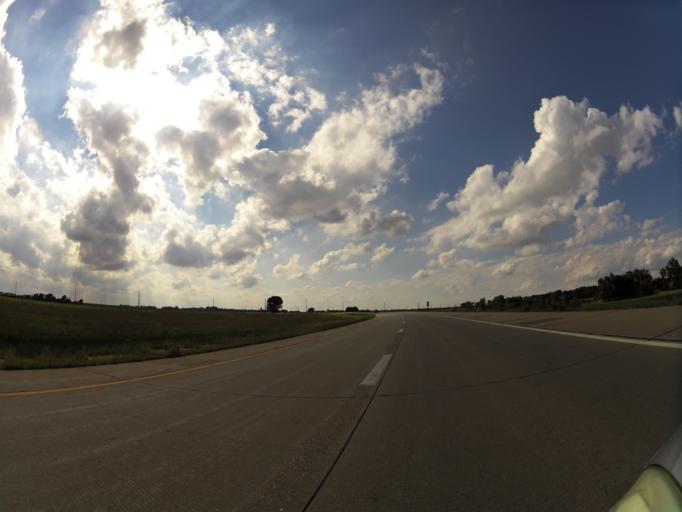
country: US
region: Kansas
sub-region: Sedgwick County
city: Colwich
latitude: 37.8216
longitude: -97.5118
